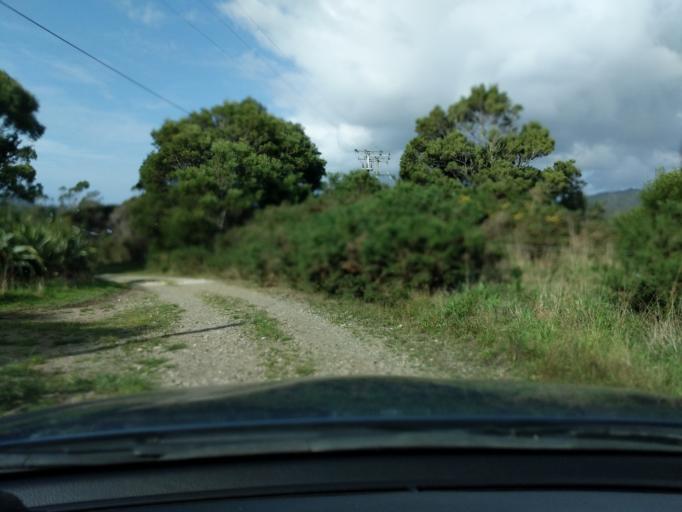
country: NZ
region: Tasman
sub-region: Tasman District
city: Takaka
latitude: -40.6512
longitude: 172.4766
